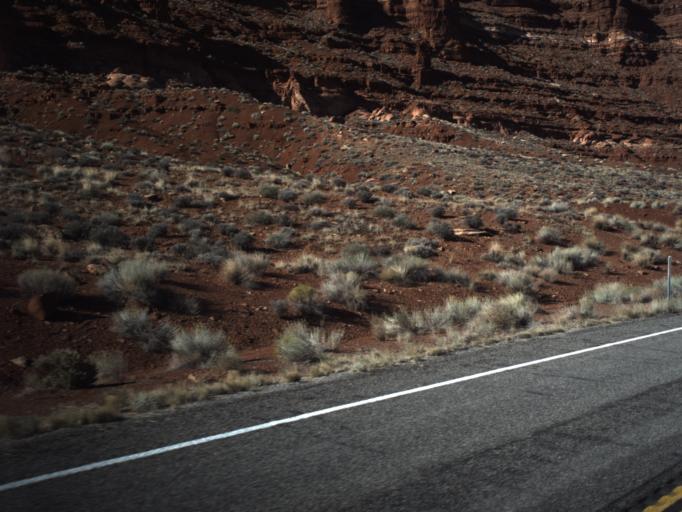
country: US
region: Utah
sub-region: San Juan County
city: Blanding
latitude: 37.8724
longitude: -110.3450
